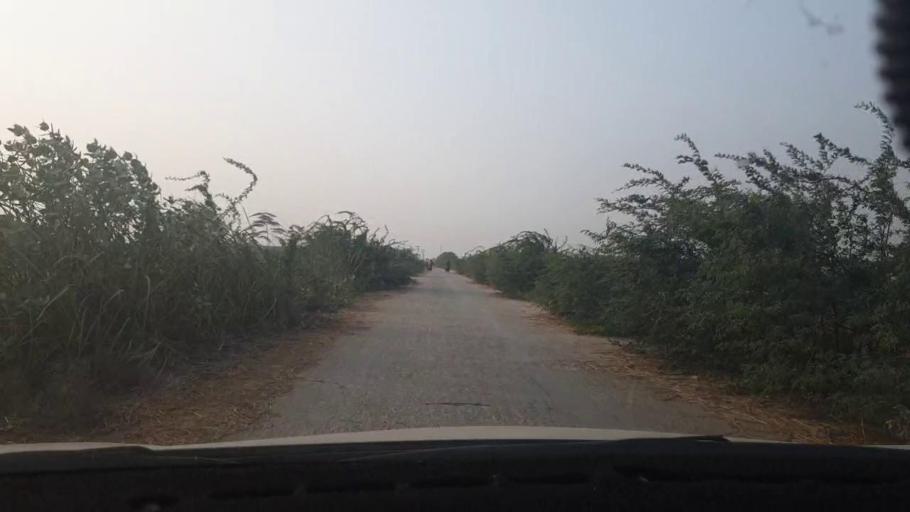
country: PK
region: Sindh
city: Bulri
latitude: 24.8526
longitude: 68.3415
